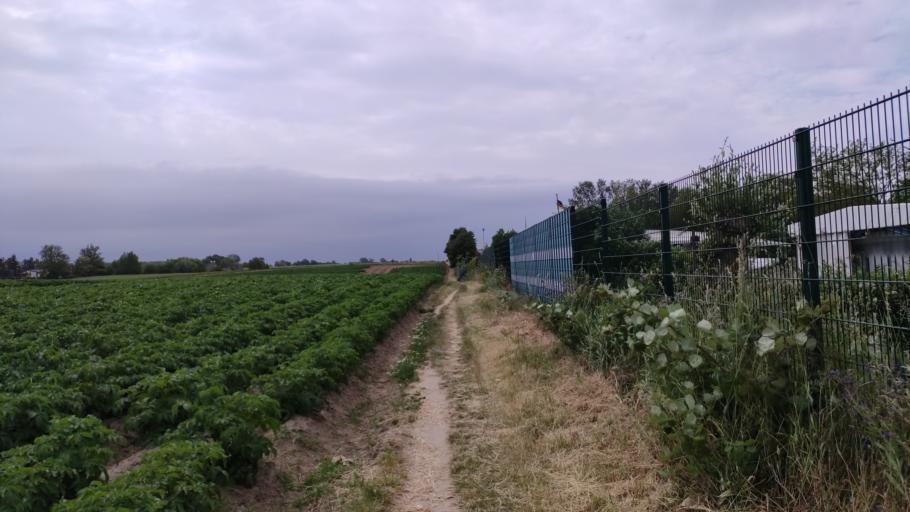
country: DE
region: Mecklenburg-Vorpommern
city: Bastorf
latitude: 54.1295
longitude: 11.6476
